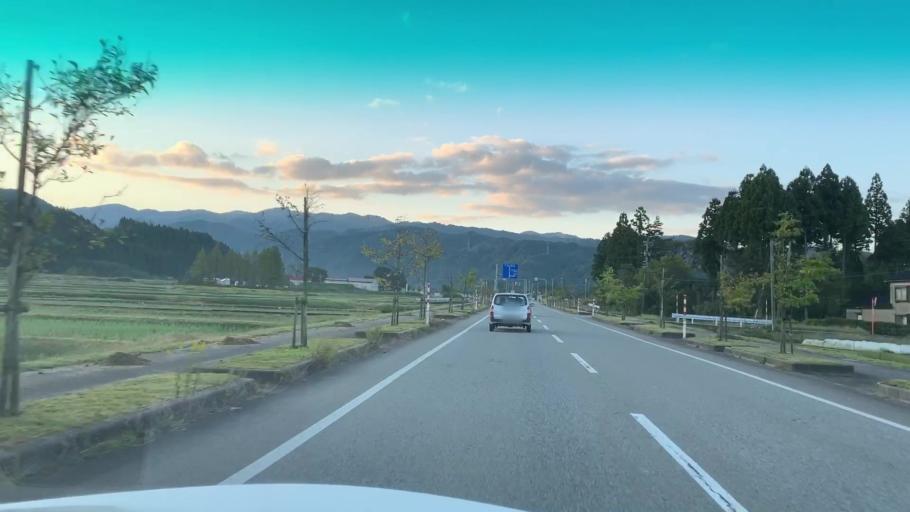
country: JP
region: Toyama
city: Kamiichi
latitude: 36.5967
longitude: 137.3271
